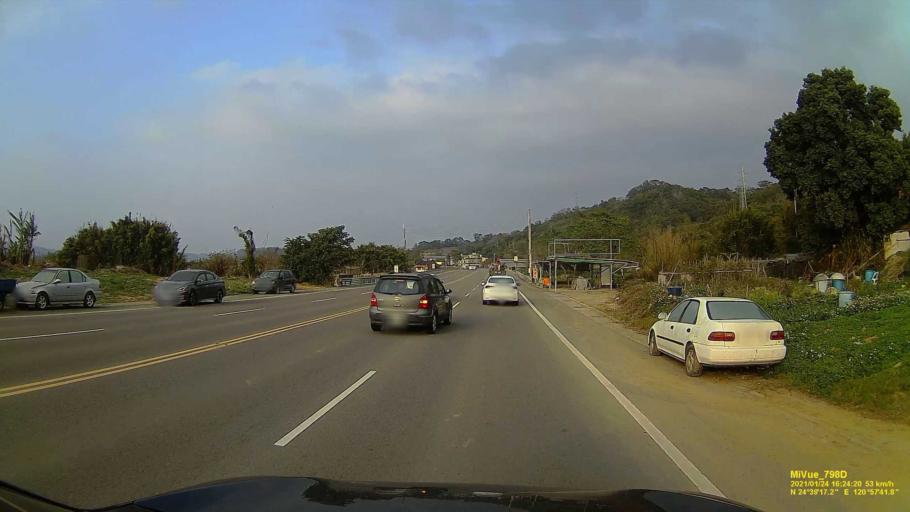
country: TW
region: Taiwan
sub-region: Hsinchu
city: Hsinchu
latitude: 24.6550
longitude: 120.9618
